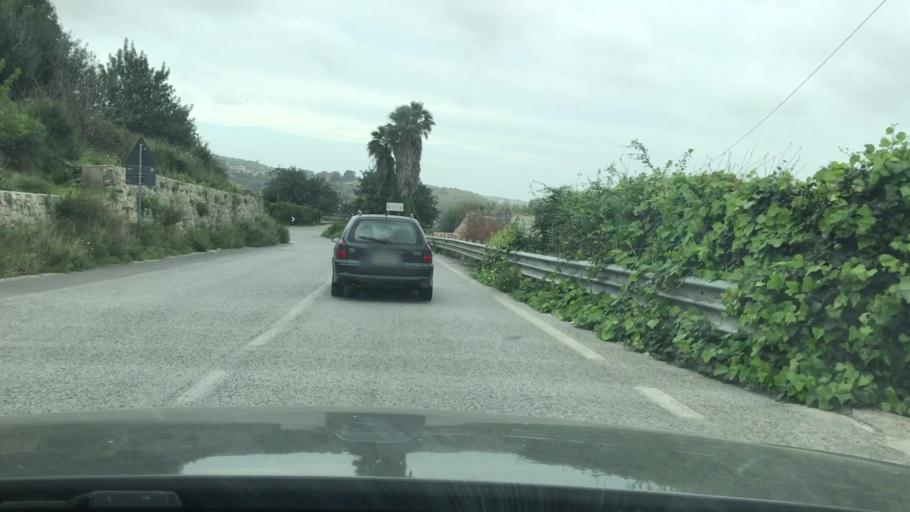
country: IT
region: Sicily
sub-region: Ragusa
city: Scicli
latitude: 36.7976
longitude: 14.7097
